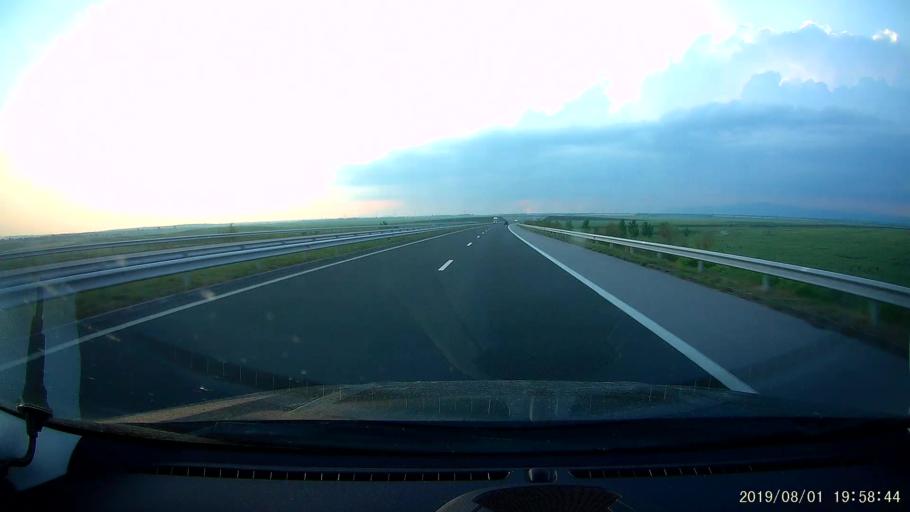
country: BG
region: Yambol
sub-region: Obshtina Straldzha
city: Straldzha
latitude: 42.5459
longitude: 26.7544
